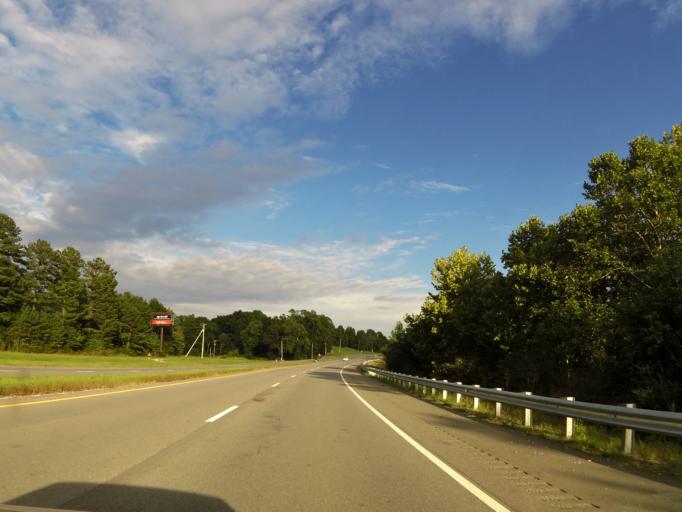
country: US
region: Alabama
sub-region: Lauderdale County
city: Rogersville
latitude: 34.8329
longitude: -87.3224
